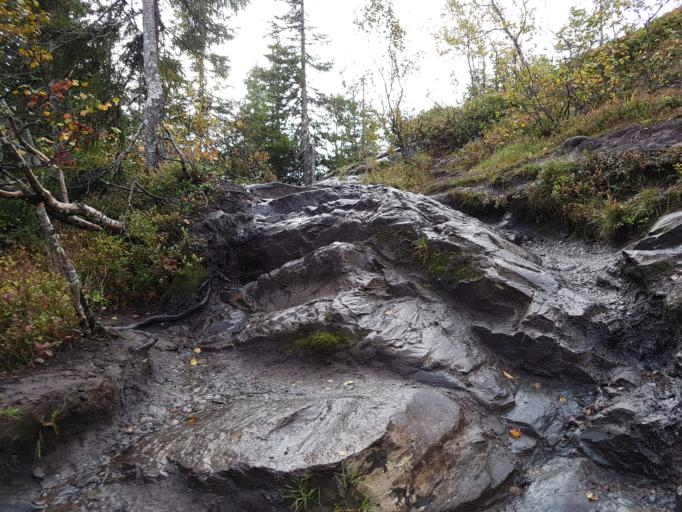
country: NO
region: Sor-Trondelag
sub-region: Melhus
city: Melhus
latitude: 63.4058
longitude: 10.2054
